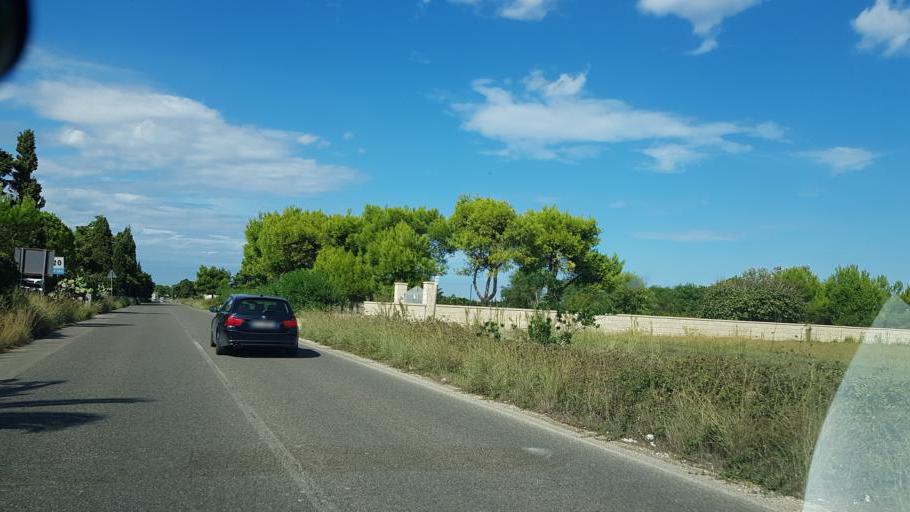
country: IT
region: Apulia
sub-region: Provincia di Lecce
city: Borgagne
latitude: 40.2591
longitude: 18.4356
